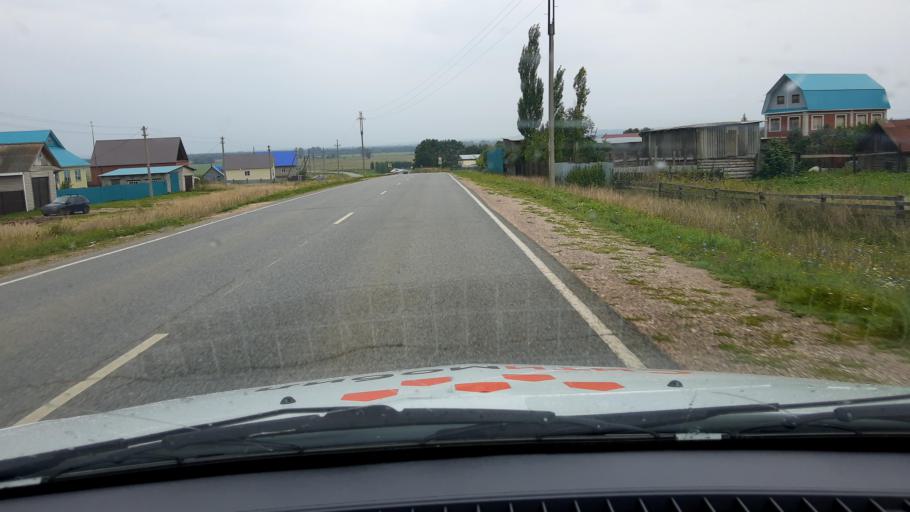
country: RU
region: Bashkortostan
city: Krasnaya Gorka
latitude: 55.1826
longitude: 56.6764
